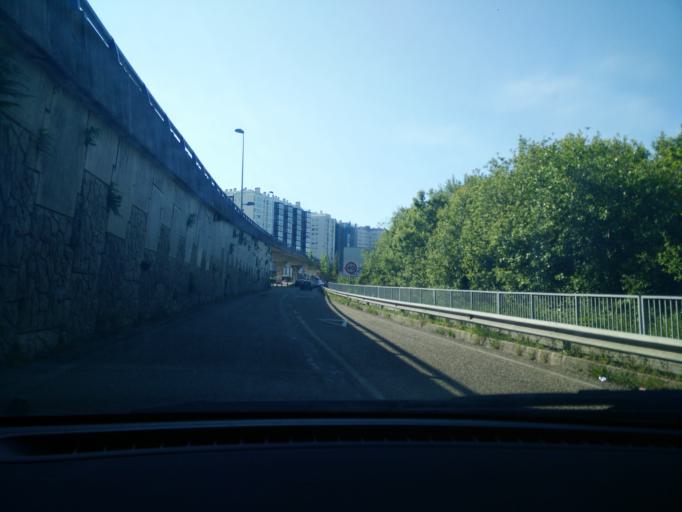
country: ES
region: Galicia
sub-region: Provincia de Pontevedra
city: Vigo
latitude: 42.2097
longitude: -8.7512
